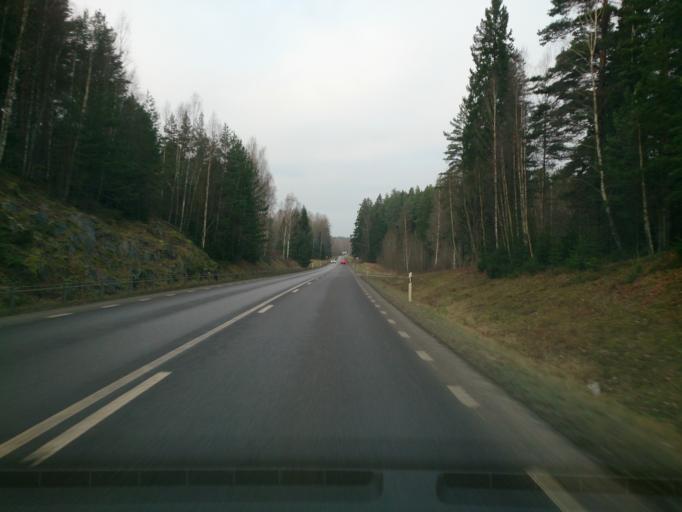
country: SE
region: OEstergoetland
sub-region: Atvidabergs Kommun
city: Atvidaberg
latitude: 58.2434
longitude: 15.9337
